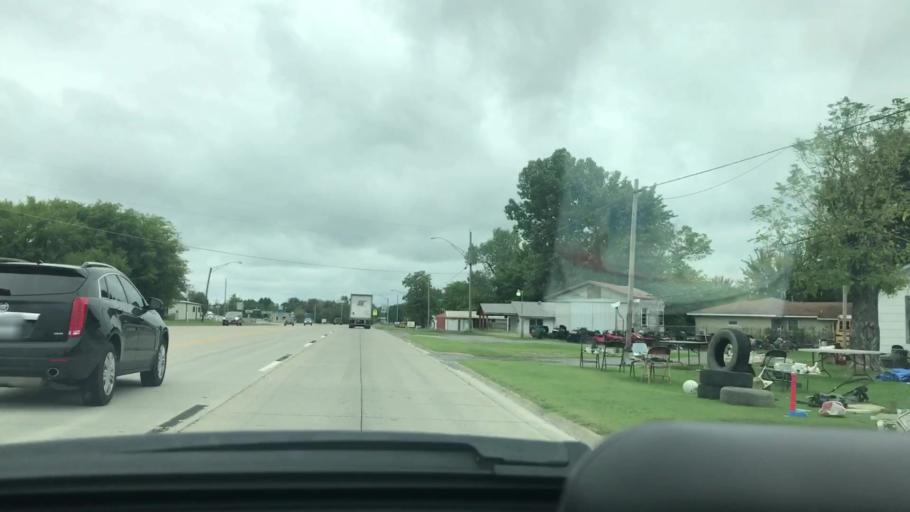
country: US
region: Oklahoma
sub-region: Pittsburg County
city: McAlester
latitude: 34.8248
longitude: -95.8468
